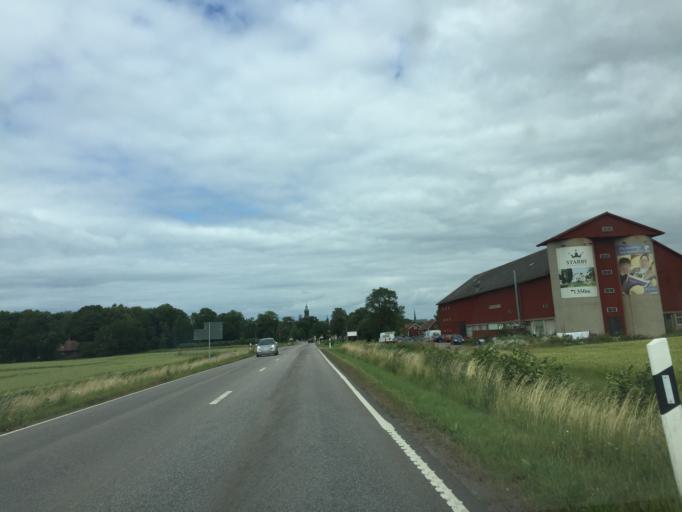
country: SE
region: OEstergoetland
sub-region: Vadstena Kommun
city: Vadstena
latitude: 58.4371
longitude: 14.8782
